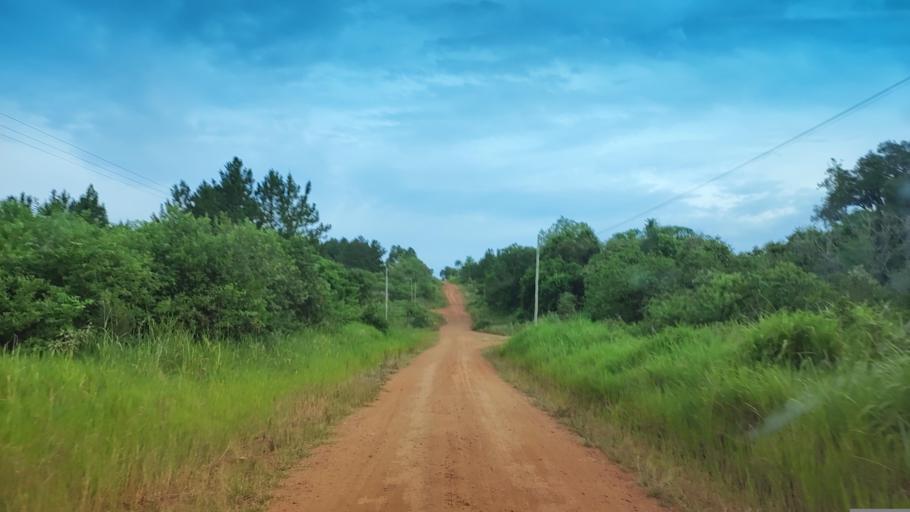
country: AR
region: Misiones
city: Gobernador Roca
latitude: -27.1578
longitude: -55.4640
